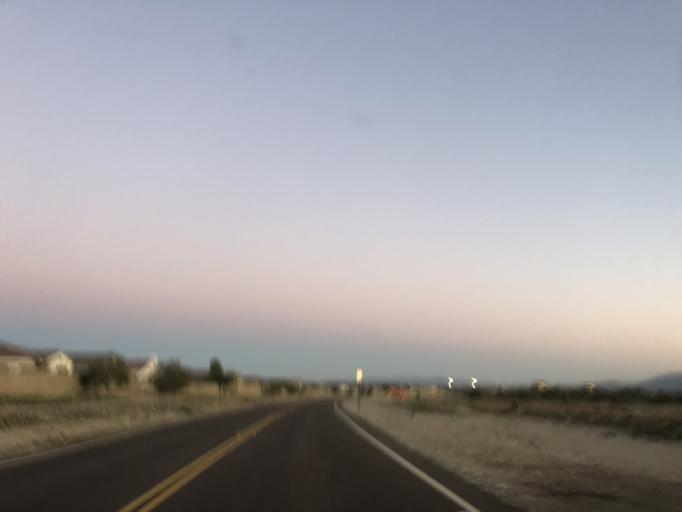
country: US
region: Arizona
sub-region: Maricopa County
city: Citrus Park
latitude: 33.5021
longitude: -112.5083
